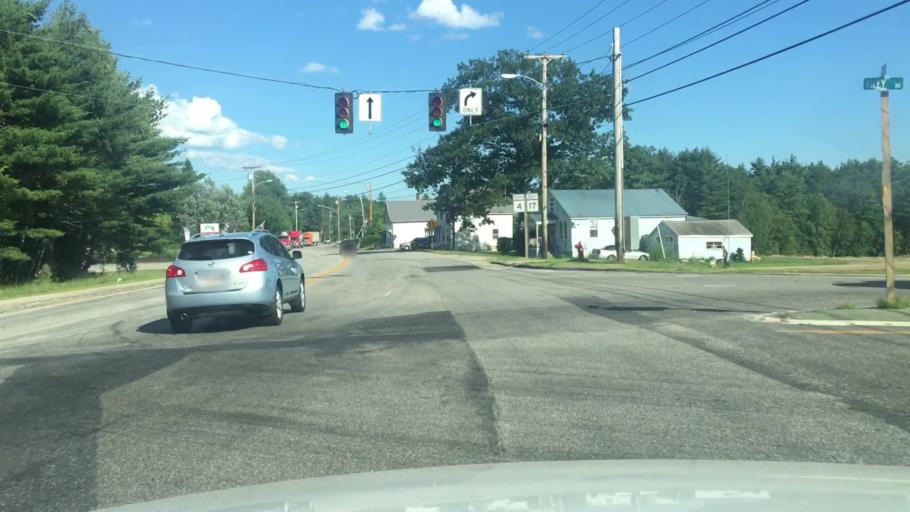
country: US
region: Maine
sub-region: Franklin County
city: Jay
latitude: 44.5032
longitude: -70.2147
